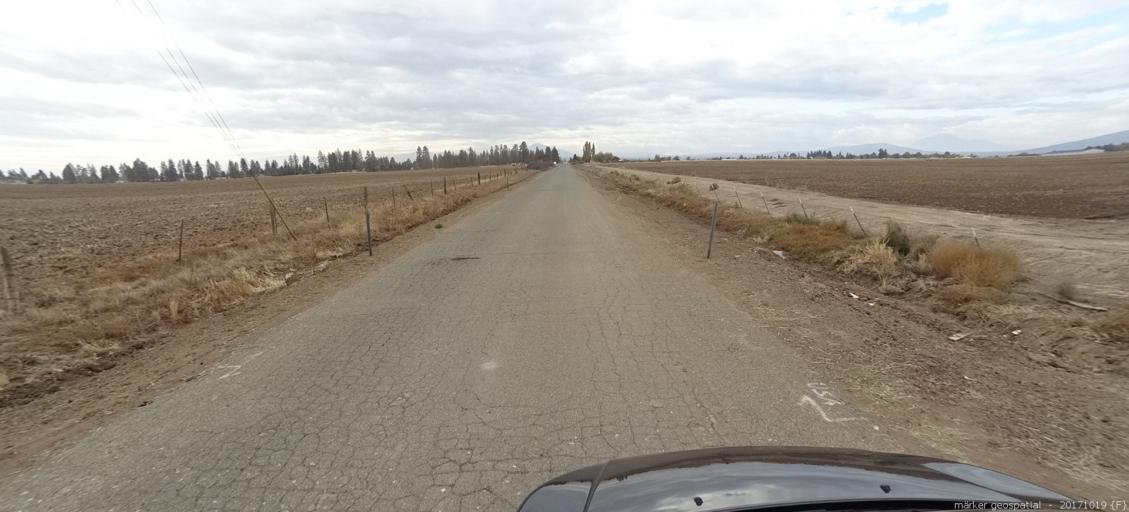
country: US
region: California
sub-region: Shasta County
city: Burney
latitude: 41.0652
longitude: -121.3891
